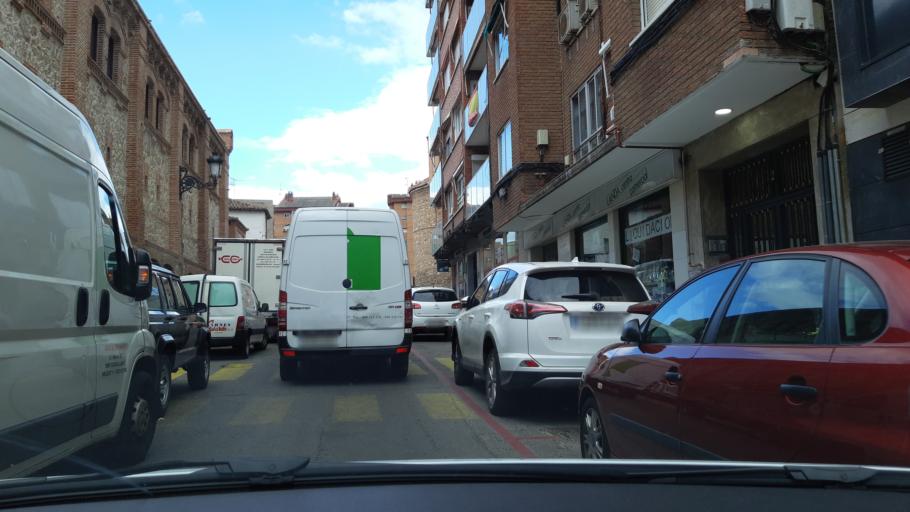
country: ES
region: Castille-La Mancha
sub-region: Provincia de Guadalajara
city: Guadalajara
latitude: 40.6331
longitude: -3.1682
